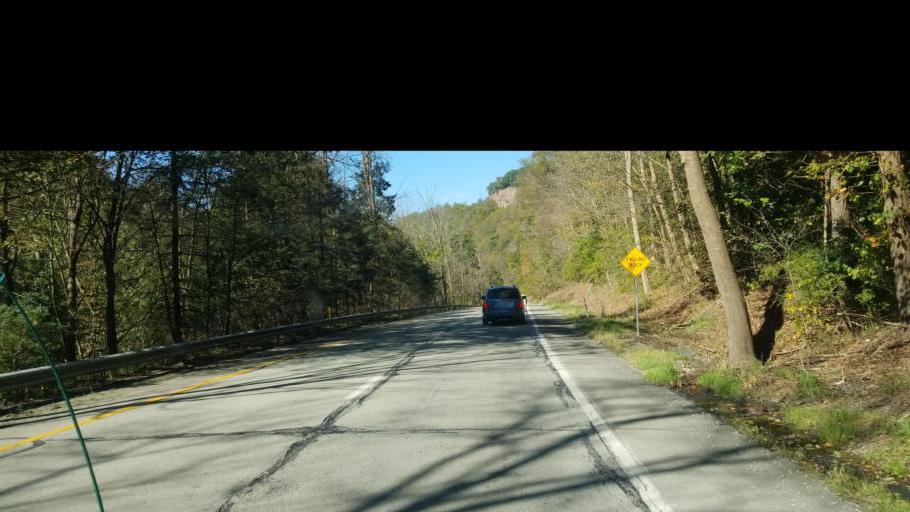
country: US
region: Pennsylvania
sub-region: Westmoreland County
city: Ligonier
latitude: 40.2690
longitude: -79.2946
